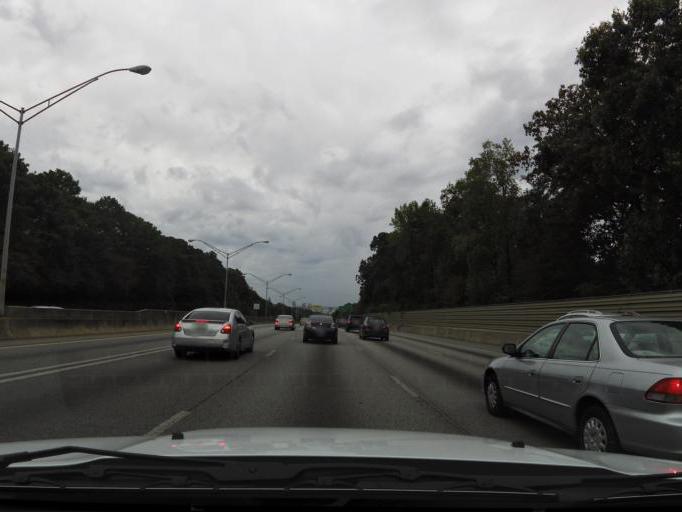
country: US
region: Georgia
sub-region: Cobb County
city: Vinings
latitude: 33.8363
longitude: -84.4293
